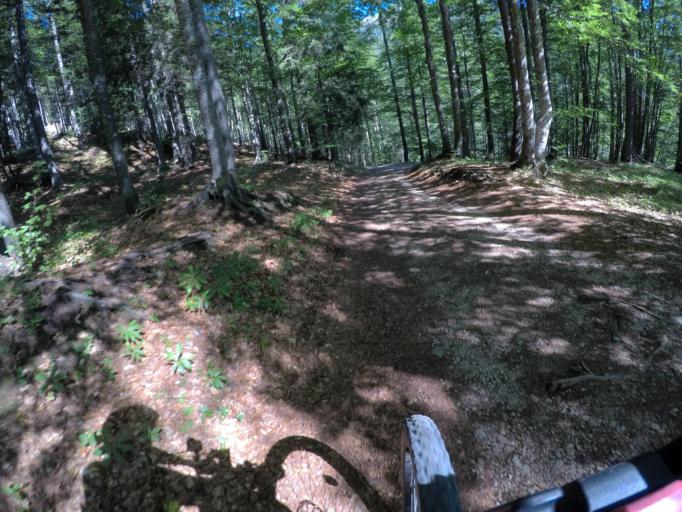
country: IT
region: Friuli Venezia Giulia
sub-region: Provincia di Udine
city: Malborghetto
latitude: 46.4589
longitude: 13.4530
